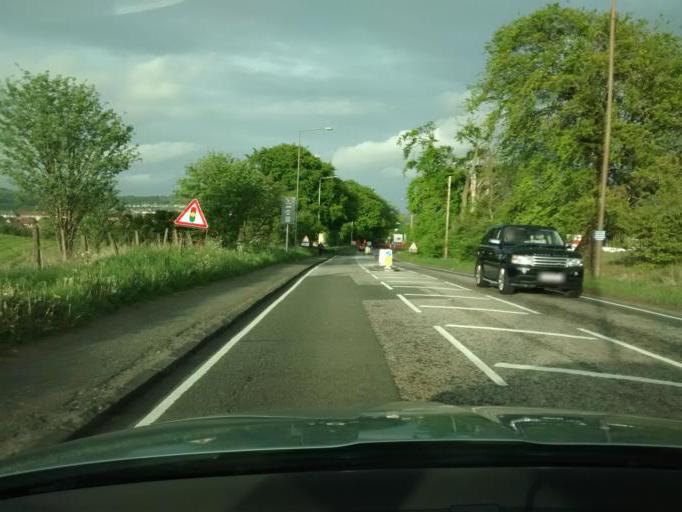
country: GB
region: Scotland
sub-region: West Lothian
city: Bathgate
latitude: 55.9003
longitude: -3.6673
